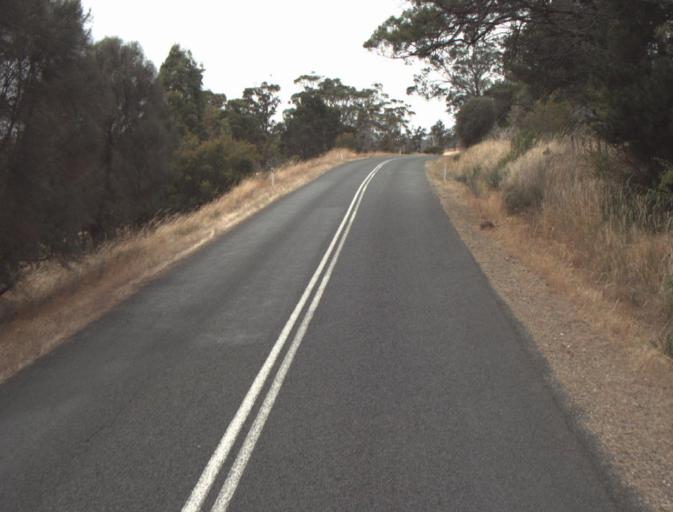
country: AU
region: Tasmania
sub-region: Northern Midlands
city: Evandale
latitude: -41.5135
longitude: 147.2977
